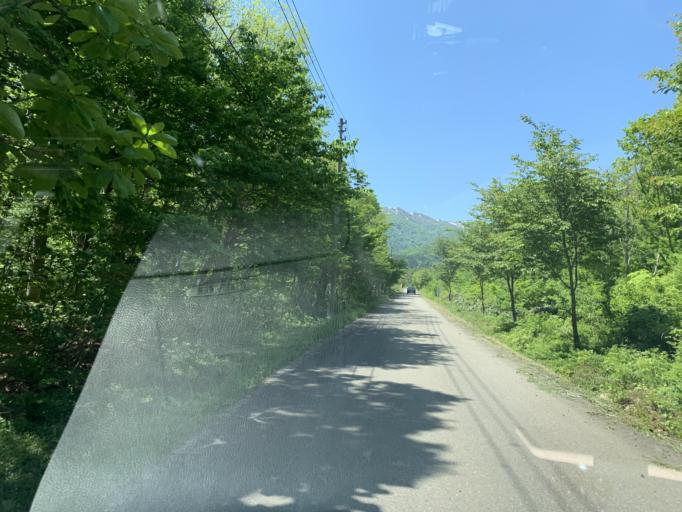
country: JP
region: Iwate
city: Shizukuishi
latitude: 39.5456
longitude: 140.8234
